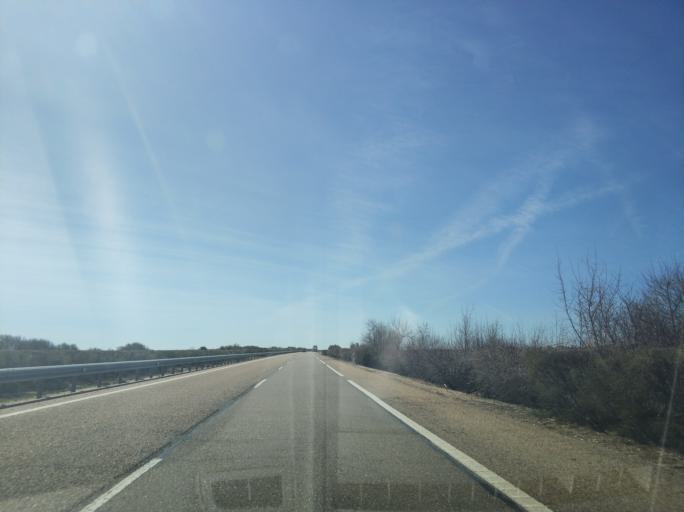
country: ES
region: Castille and Leon
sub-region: Provincia de Valladolid
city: Alaejos
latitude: 41.2865
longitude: -5.2424
